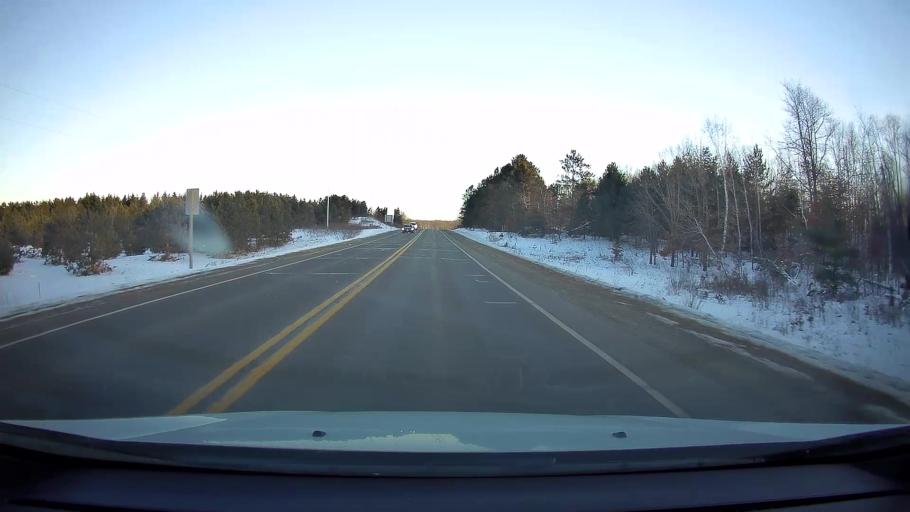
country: US
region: Wisconsin
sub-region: Barron County
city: Turtle Lake
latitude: 45.4036
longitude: -92.1403
